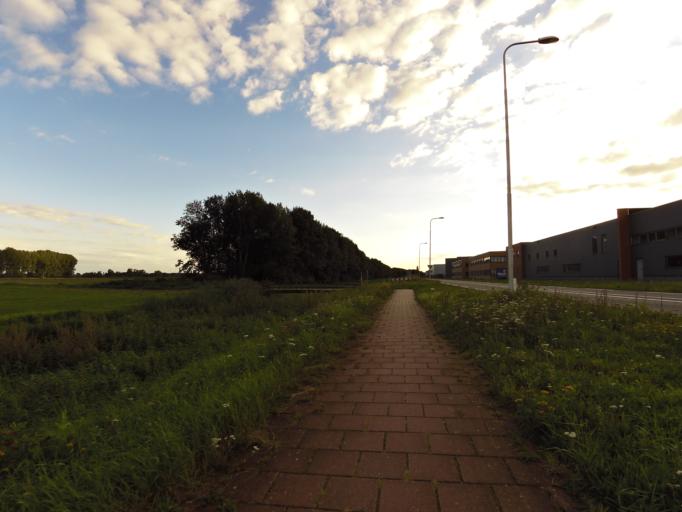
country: NL
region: Gelderland
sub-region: Gemeente Montferland
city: s-Heerenberg
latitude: 51.8738
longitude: 6.2688
